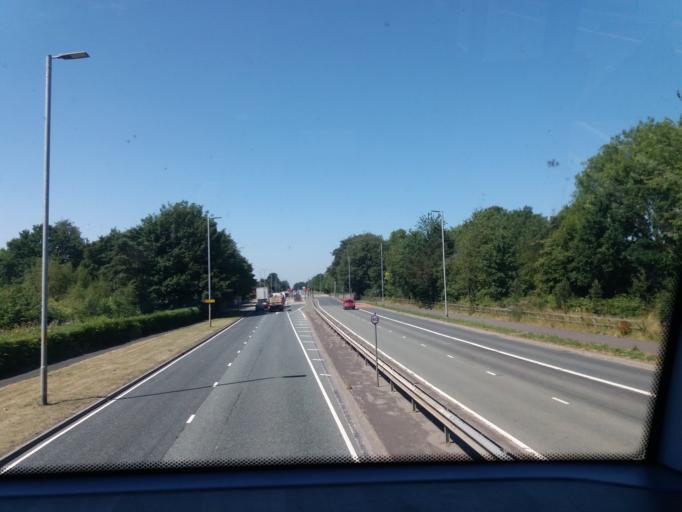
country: GB
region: England
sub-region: City and Borough of Salford
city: Walkden
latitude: 53.5081
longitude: -2.4065
